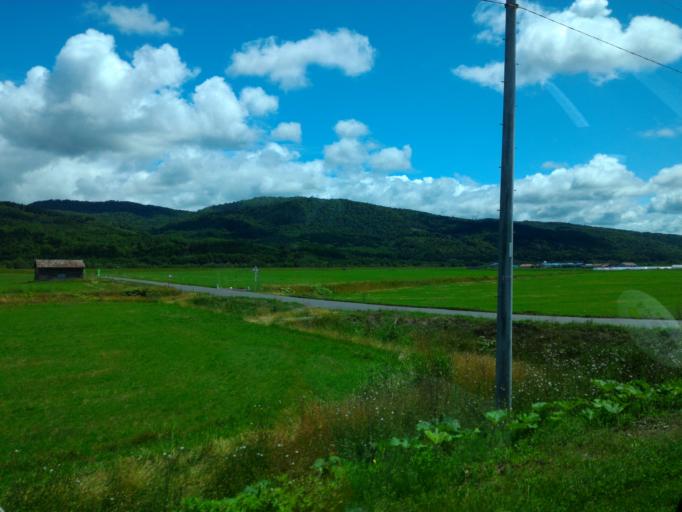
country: JP
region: Hokkaido
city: Nayoro
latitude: 44.5708
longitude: 142.3140
